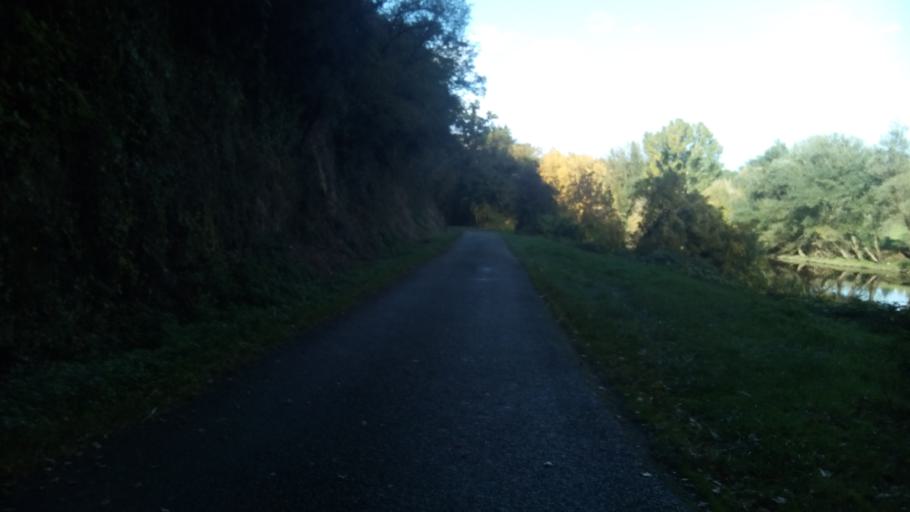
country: FR
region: Midi-Pyrenees
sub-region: Departement du Lot
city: Cajarc
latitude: 44.4700
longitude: 1.8297
